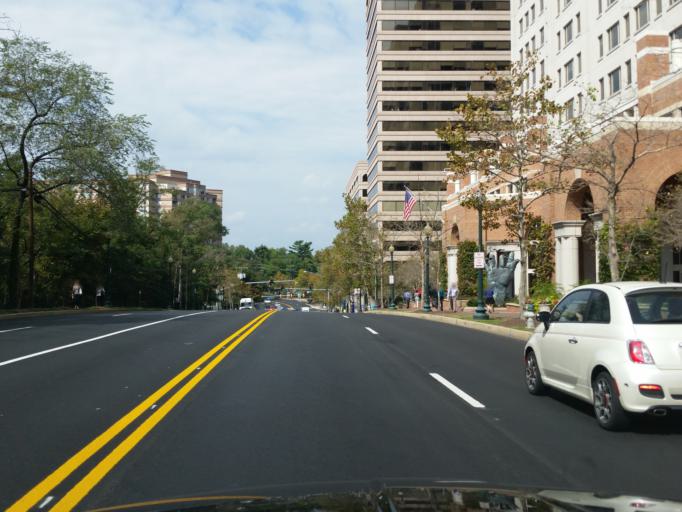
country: US
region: Maryland
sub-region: Montgomery County
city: Silver Spring
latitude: 38.9920
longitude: -77.0307
